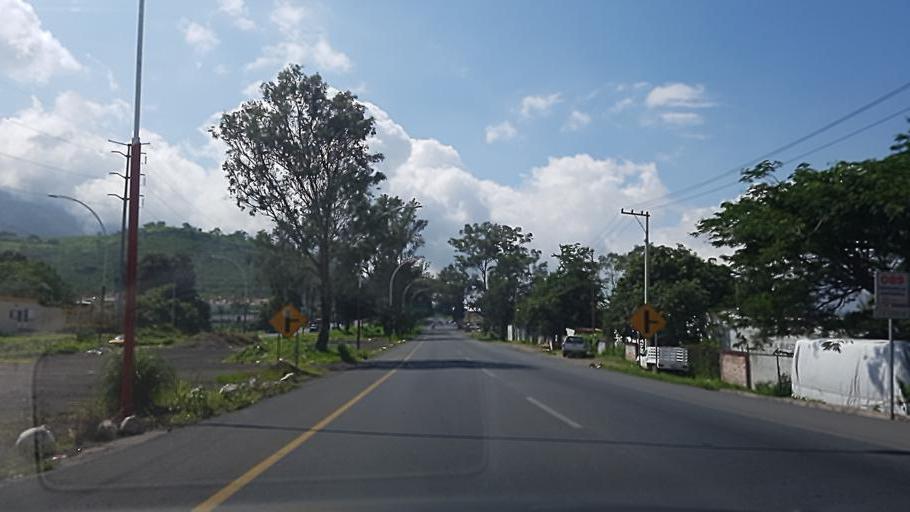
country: MX
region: Nayarit
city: Xalisco
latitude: 21.4777
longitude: -104.8955
